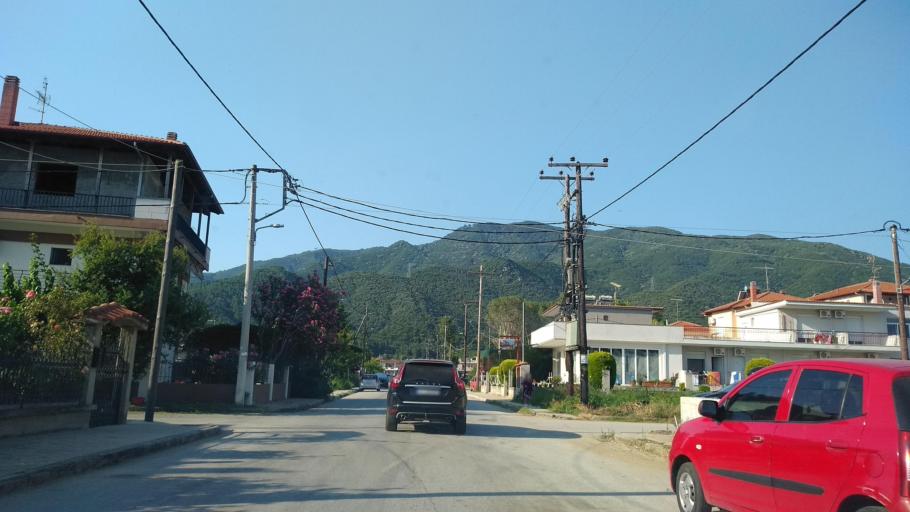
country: GR
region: Central Macedonia
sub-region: Nomos Thessalonikis
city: Stavros
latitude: 40.6684
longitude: 23.6914
